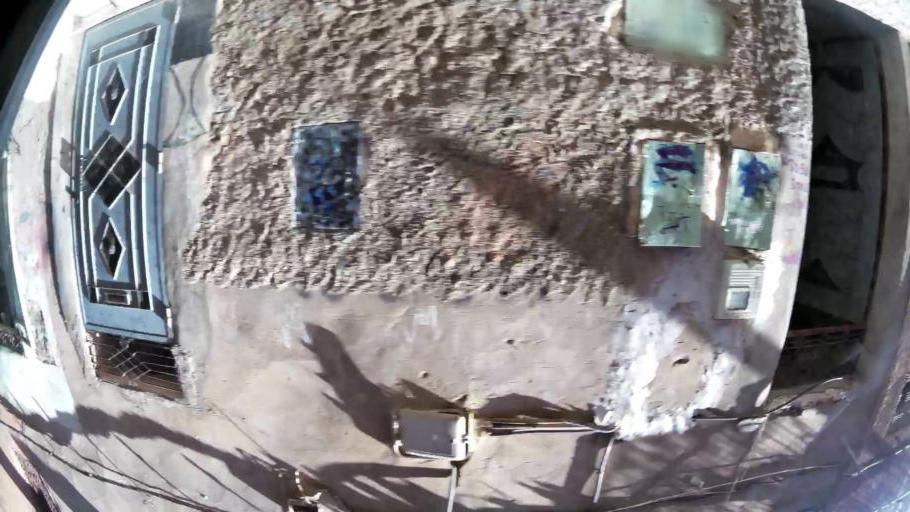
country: MA
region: Marrakech-Tensift-Al Haouz
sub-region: Marrakech
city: Marrakesh
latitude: 31.6122
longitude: -7.9588
